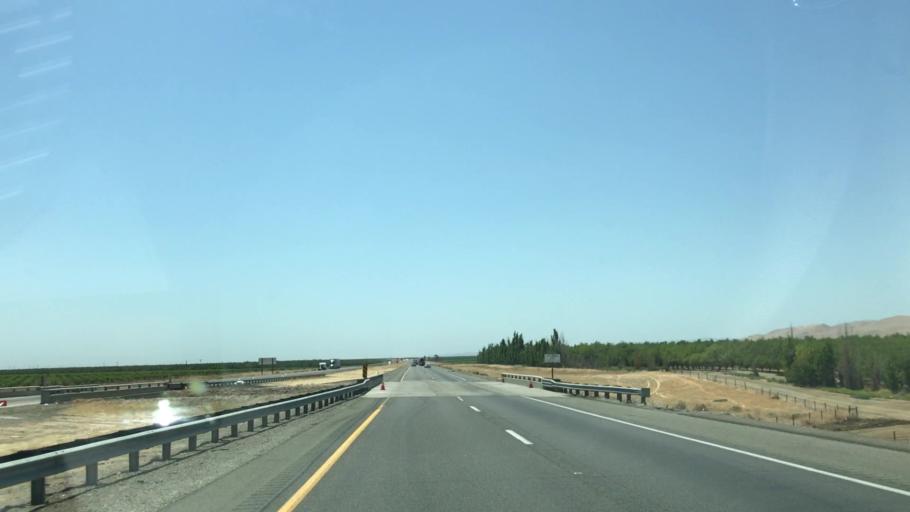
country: US
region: California
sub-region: Merced County
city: South Dos Palos
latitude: 36.8054
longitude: -120.7435
